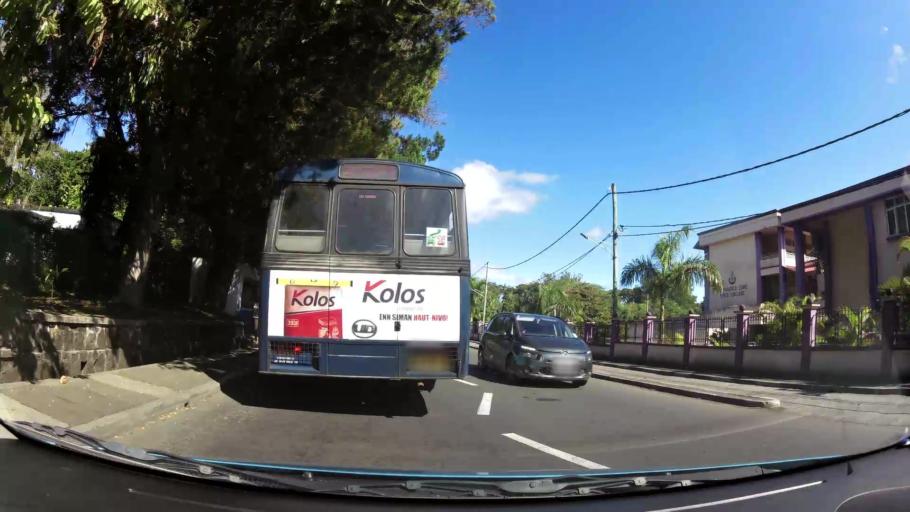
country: MU
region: Plaines Wilhems
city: Vacoas
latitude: -20.2978
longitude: 57.4951
